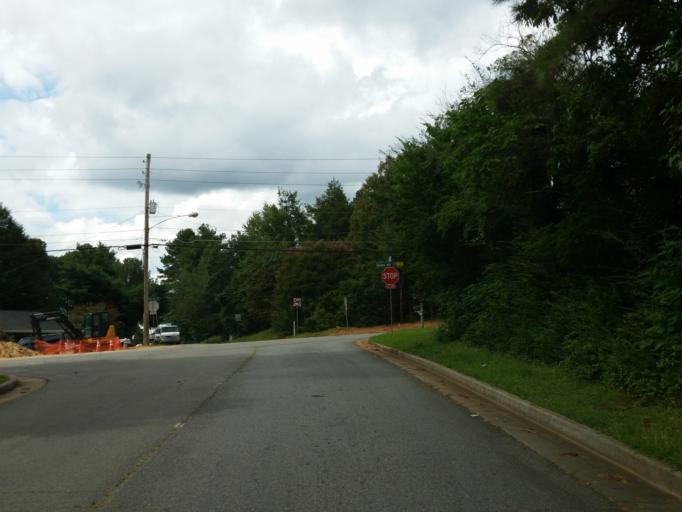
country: US
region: Georgia
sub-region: Cobb County
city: Marietta
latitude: 33.9615
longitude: -84.5260
